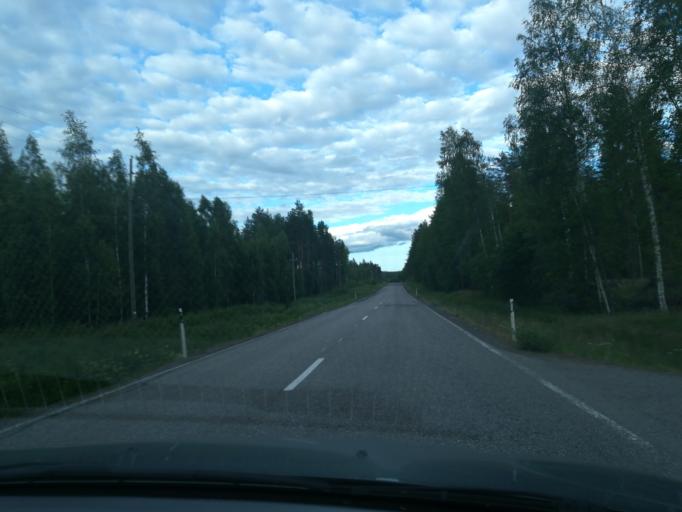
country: FI
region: Southern Savonia
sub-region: Mikkeli
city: Puumala
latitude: 61.5602
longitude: 28.0169
